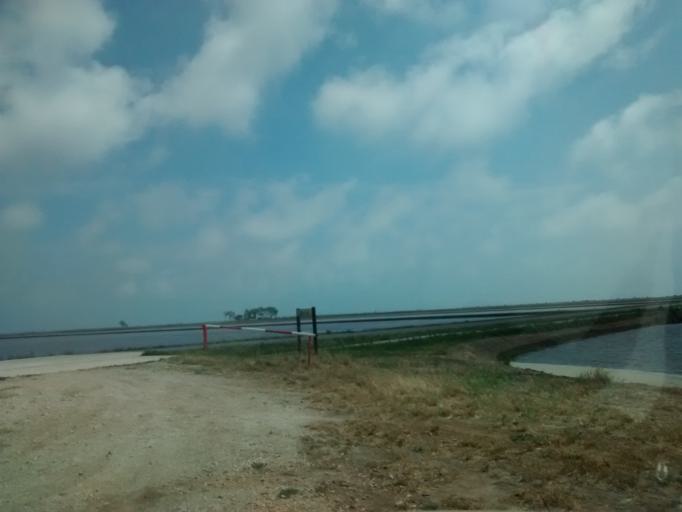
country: ES
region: Catalonia
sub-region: Provincia de Tarragona
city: Deltebre
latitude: 40.6780
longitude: 0.7989
